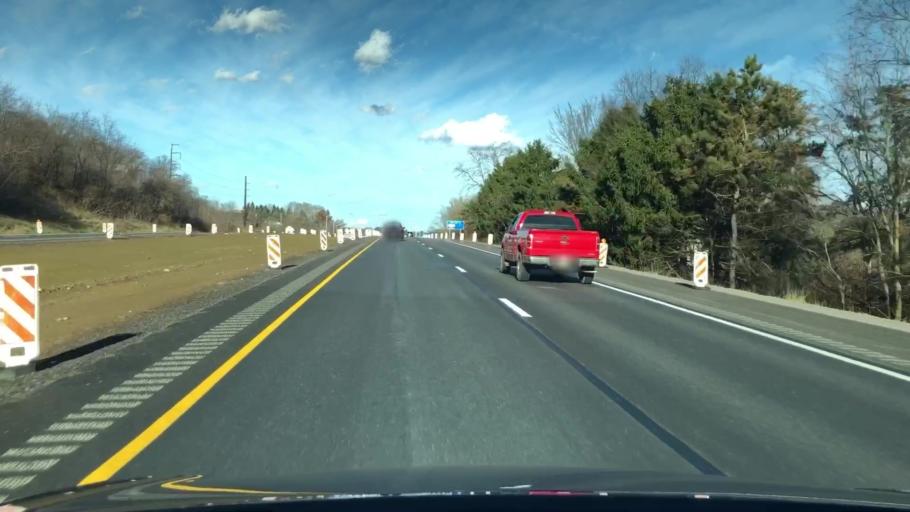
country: US
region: Pennsylvania
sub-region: Armstrong County
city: Freeport
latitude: 40.6600
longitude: -79.7209
